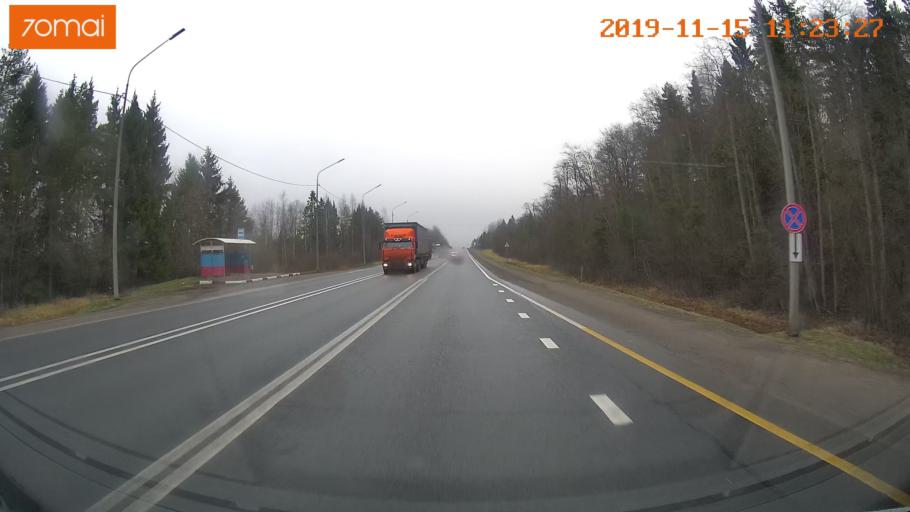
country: RU
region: Vologda
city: Molochnoye
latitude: 59.1515
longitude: 39.3820
